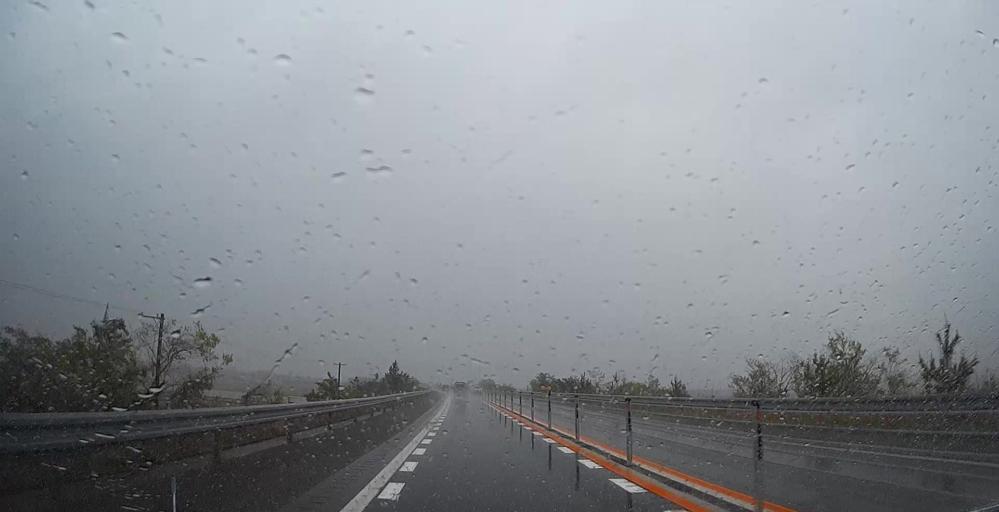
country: JP
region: Niigata
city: Shibata
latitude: 37.9772
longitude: 139.3104
